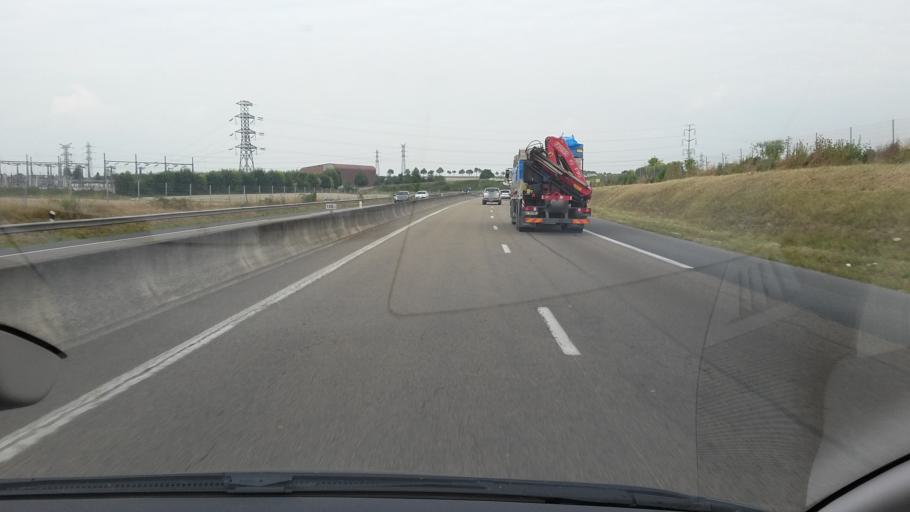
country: FR
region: Champagne-Ardenne
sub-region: Departement de la Marne
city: Cernay-les-Reims
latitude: 49.2683
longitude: 4.0870
